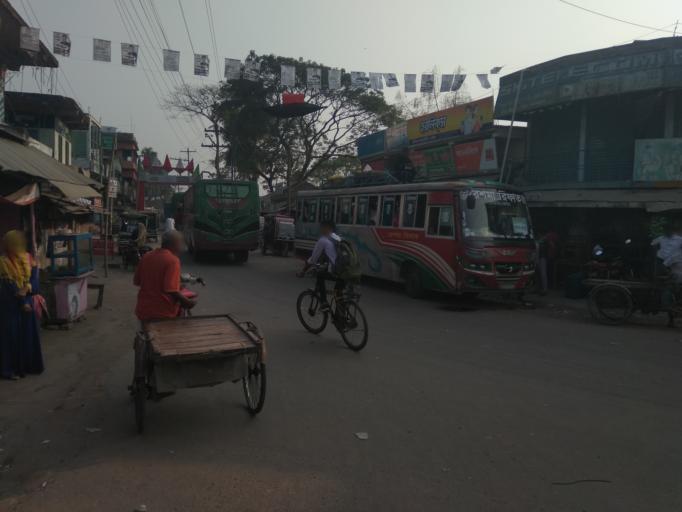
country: BD
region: Khulna
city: Kesabpur
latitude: 22.7503
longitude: 89.2563
